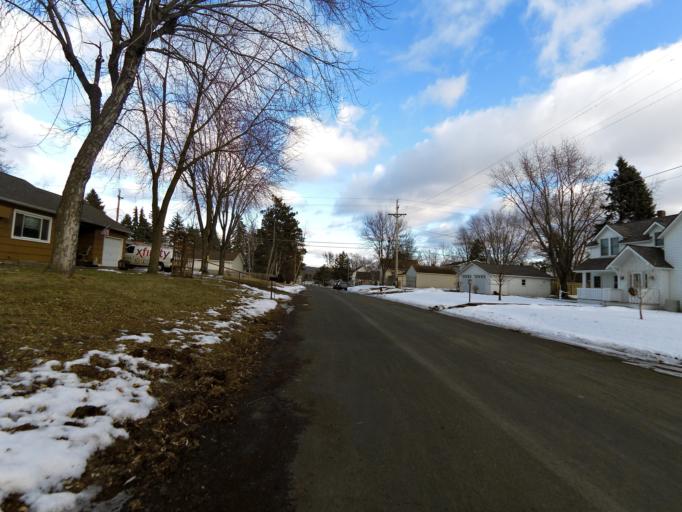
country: US
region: Minnesota
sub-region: Washington County
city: Bayport
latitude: 45.0154
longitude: -92.7823
